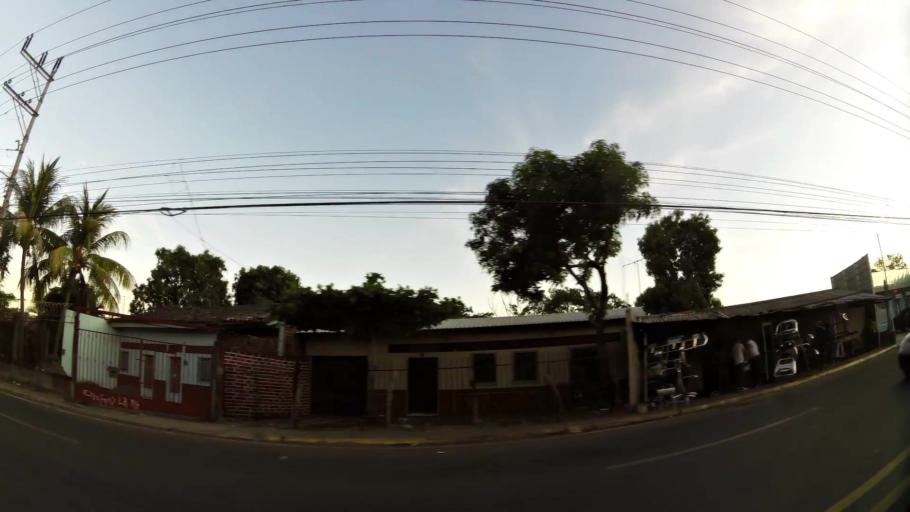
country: SV
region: San Miguel
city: San Miguel
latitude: 13.4878
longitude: -88.1848
